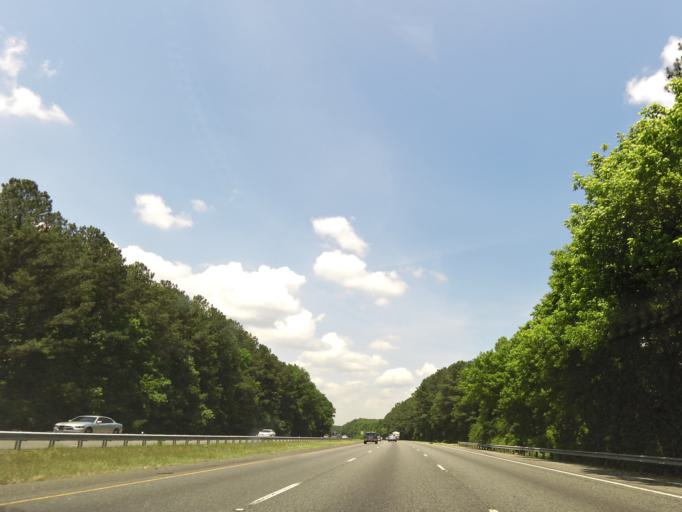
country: US
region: Georgia
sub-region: Butts County
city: Indian Springs
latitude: 33.1734
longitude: -84.0435
